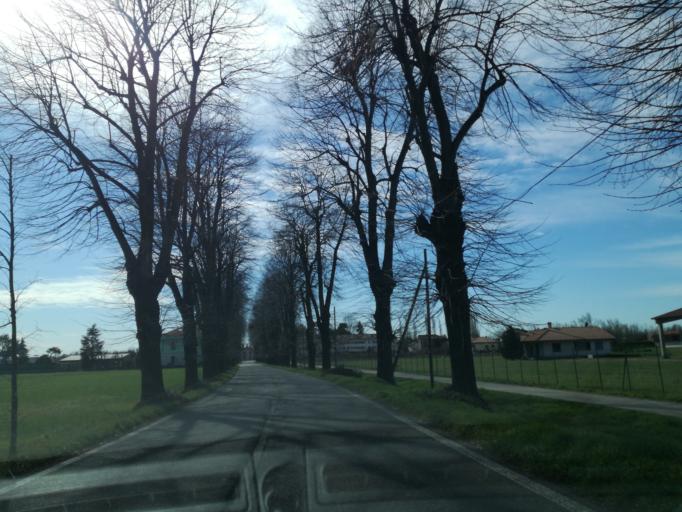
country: IT
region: Lombardy
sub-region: Provincia di Monza e Brianza
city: Villasanta
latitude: 45.6244
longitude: 9.3029
